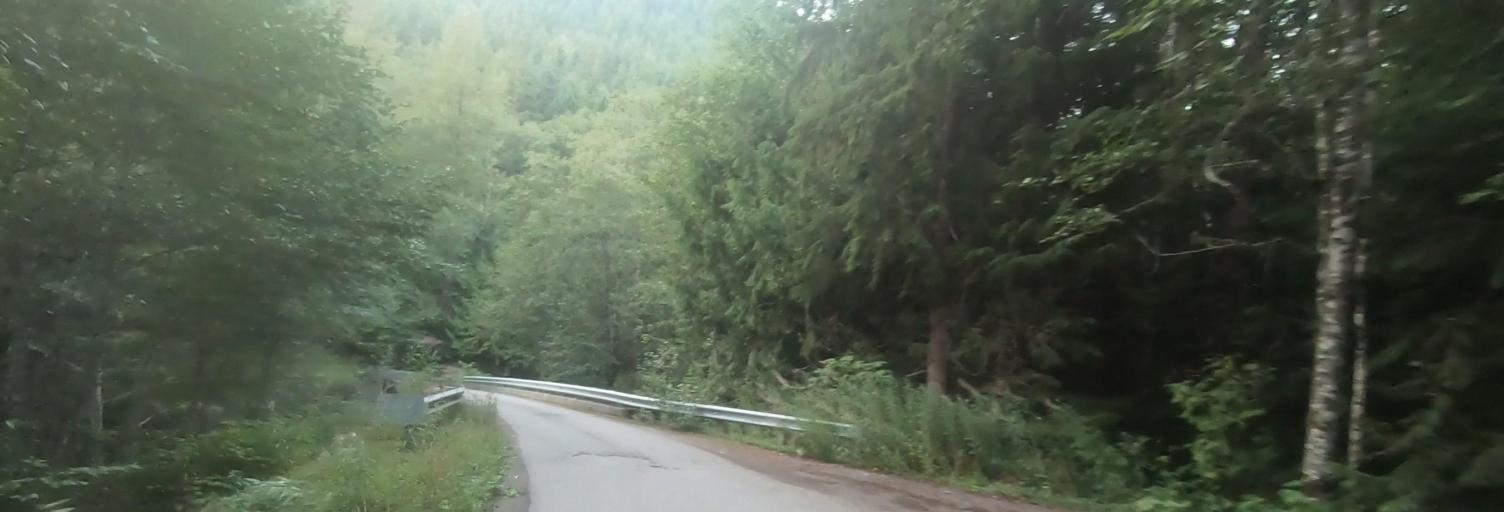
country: CA
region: British Columbia
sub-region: Fraser Valley Regional District
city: Chilliwack
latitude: 48.9504
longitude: -121.9305
